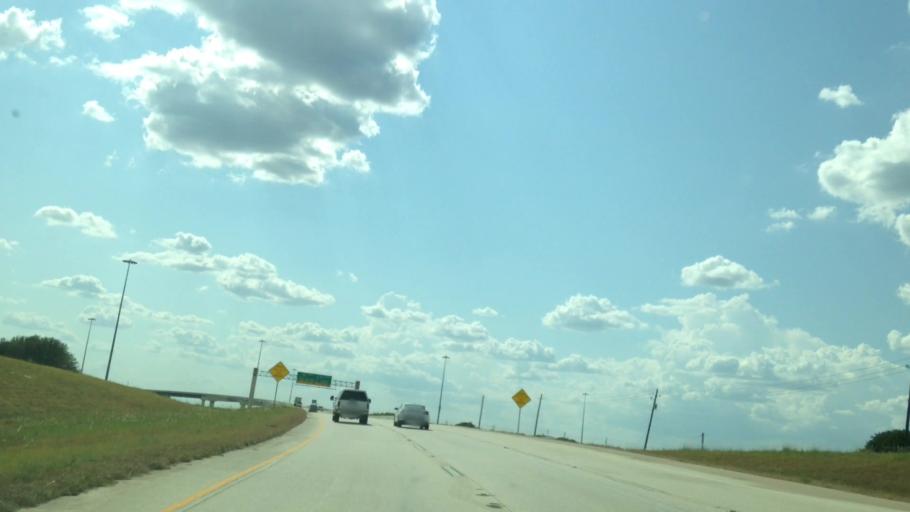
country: US
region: Texas
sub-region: Travis County
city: Onion Creek
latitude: 30.1122
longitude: -97.7991
